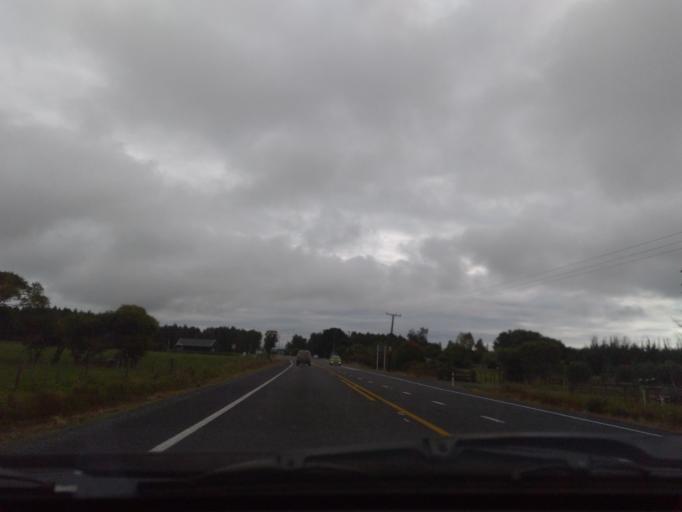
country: NZ
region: Northland
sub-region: Whangarei
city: Ruakaka
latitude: -35.9869
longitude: 174.4280
